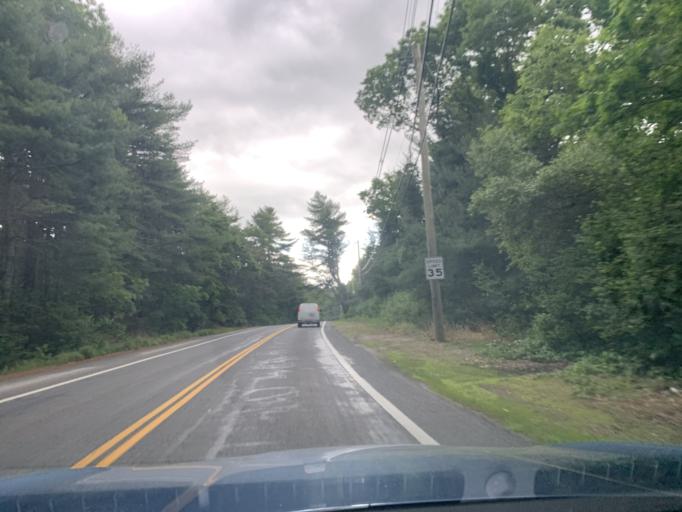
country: US
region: Rhode Island
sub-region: Kent County
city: West Greenwich
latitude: 41.6678
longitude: -71.6232
